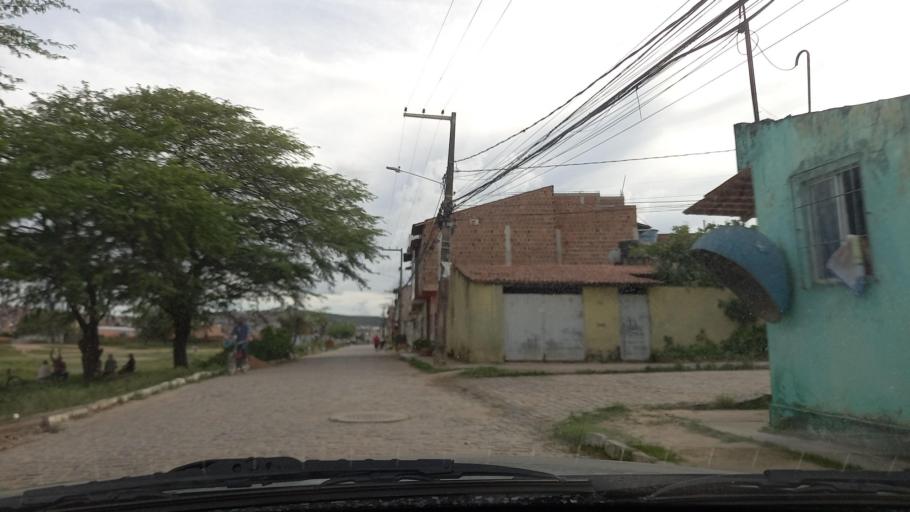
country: BR
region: Pernambuco
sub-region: Gravata
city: Gravata
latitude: -8.2017
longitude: -35.5605
